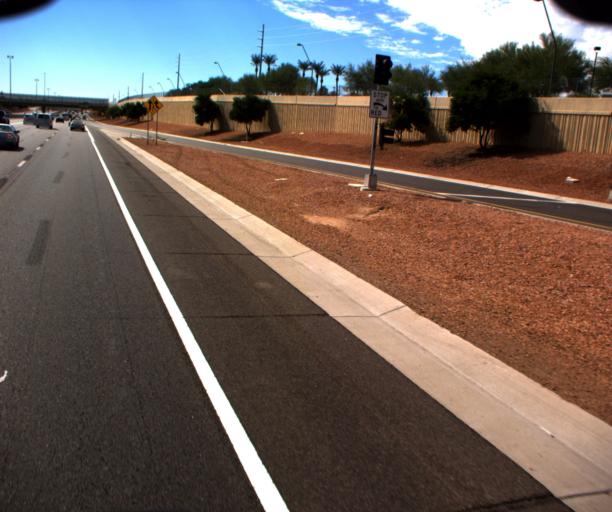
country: US
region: Arizona
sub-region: Maricopa County
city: San Carlos
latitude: 33.3460
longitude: -111.8938
